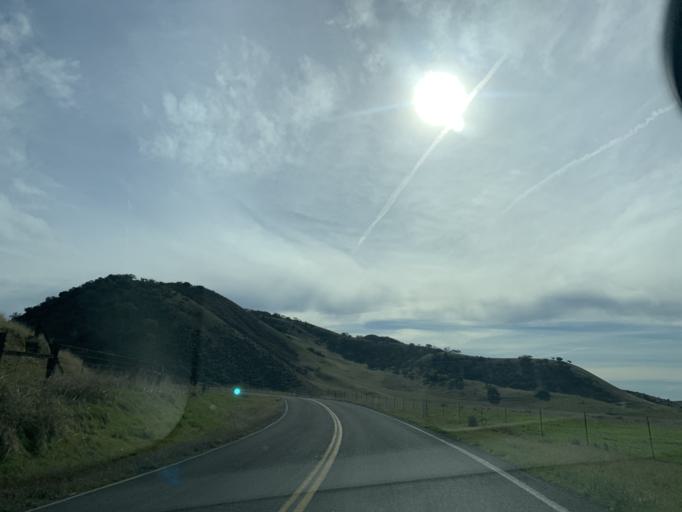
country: US
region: California
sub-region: Monterey County
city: Greenfield
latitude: 36.4482
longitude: -121.0493
